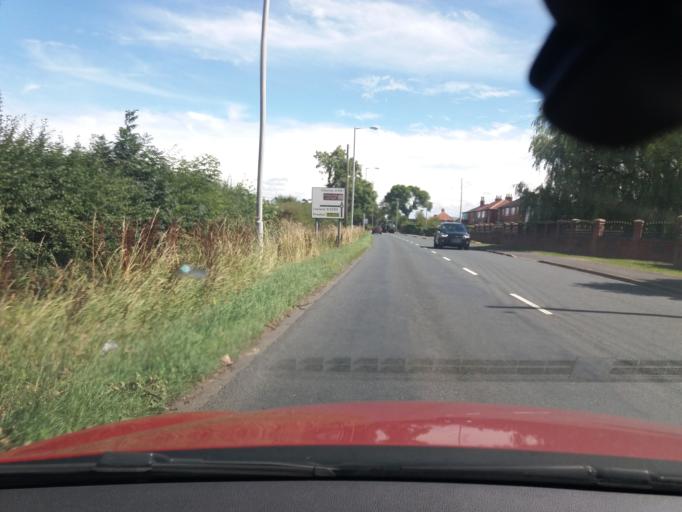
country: GB
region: England
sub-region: Lancashire
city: Croston
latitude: 53.6622
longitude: -2.7275
